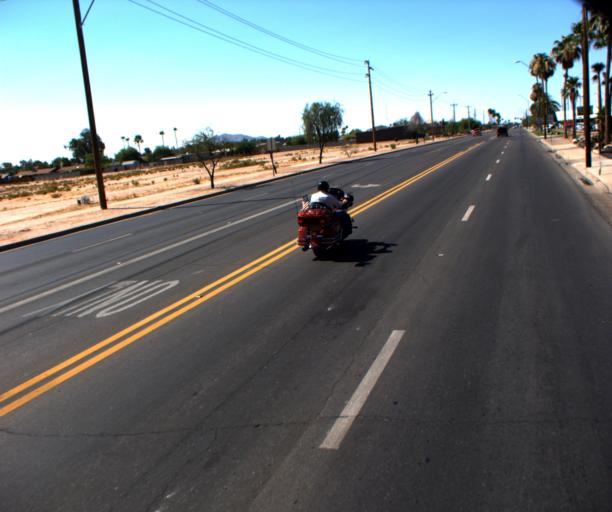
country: US
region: Arizona
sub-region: Pinal County
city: Casa Grande
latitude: 32.8939
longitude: -111.7574
